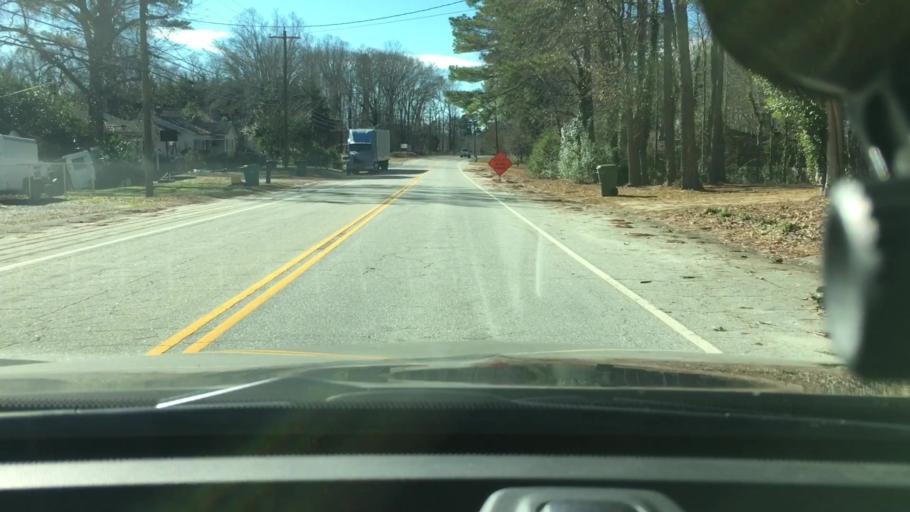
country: US
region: South Carolina
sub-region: Cherokee County
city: Gaffney
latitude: 35.0565
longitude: -81.6633
